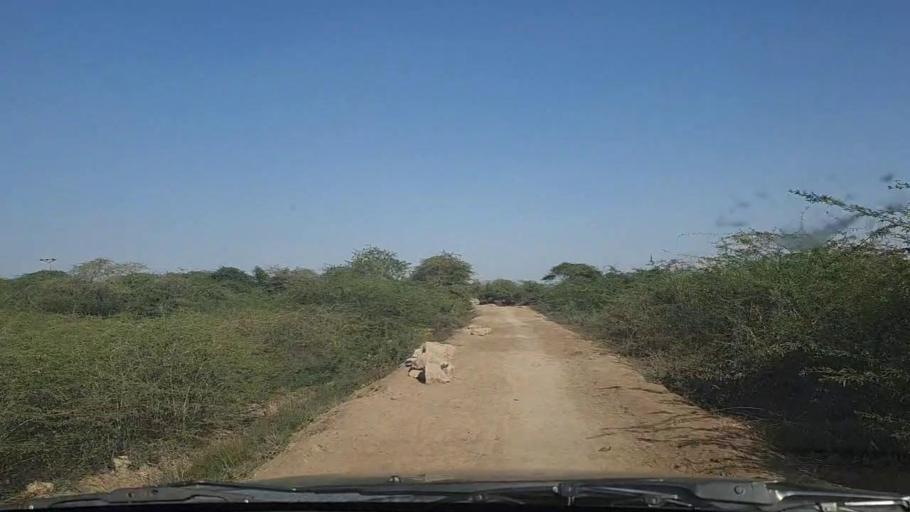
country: PK
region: Sindh
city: Chuhar Jamali
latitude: 24.3234
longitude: 67.7670
